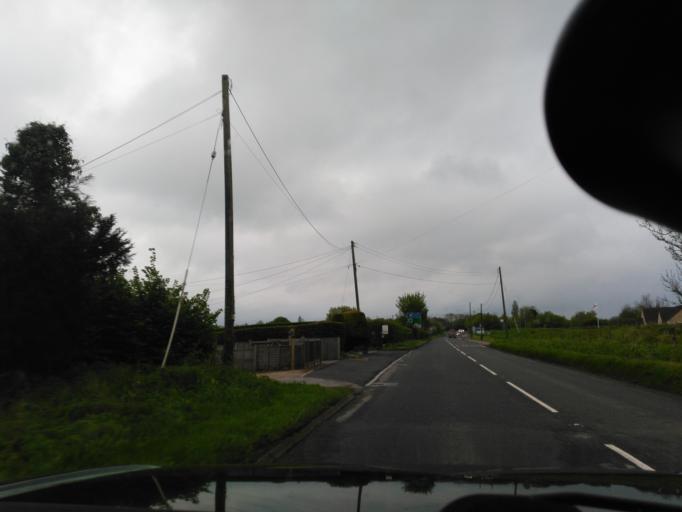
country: GB
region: England
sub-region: Wiltshire
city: Holt
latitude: 51.3342
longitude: -2.1675
